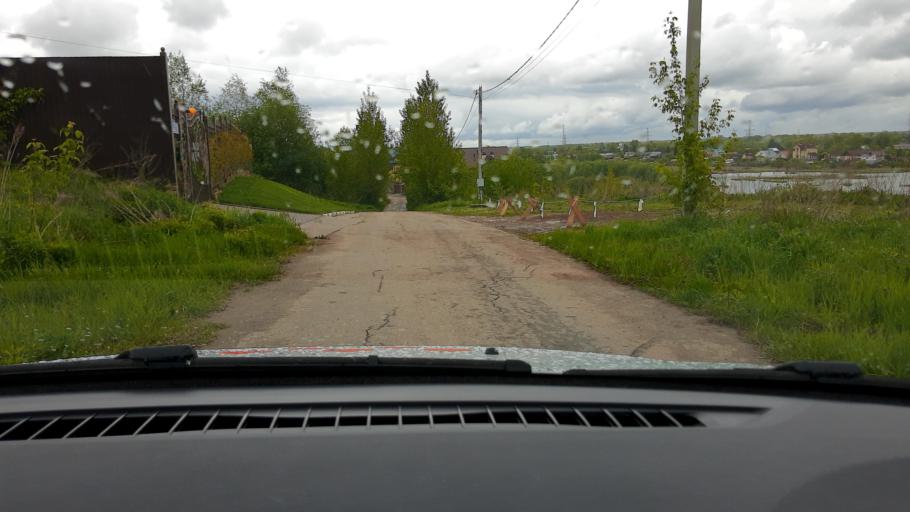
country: RU
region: Nizjnij Novgorod
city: Afonino
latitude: 56.2656
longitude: 44.0985
